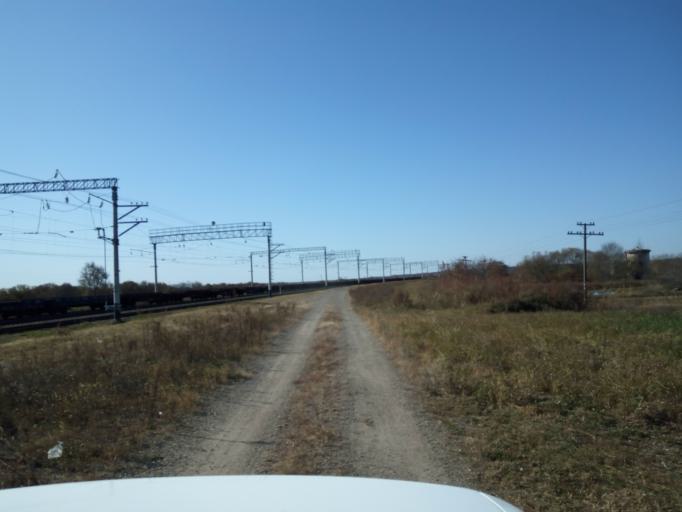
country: RU
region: Primorskiy
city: Dal'nerechensk
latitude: 45.9114
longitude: 133.7926
